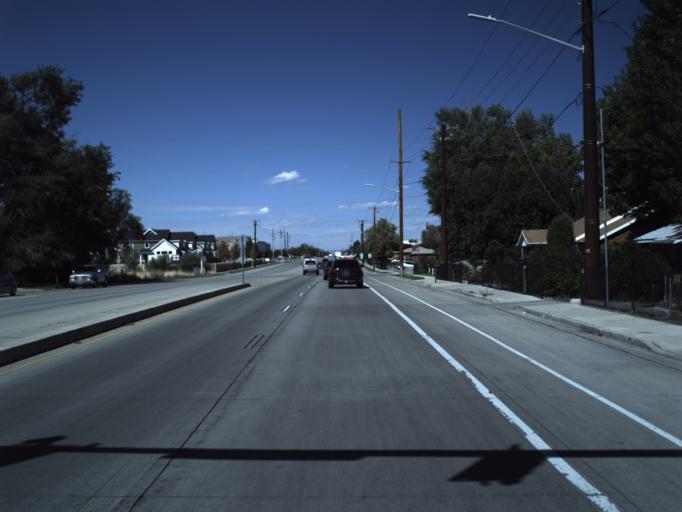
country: US
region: Utah
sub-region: Salt Lake County
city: Riverton
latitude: 40.5370
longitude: -111.9386
